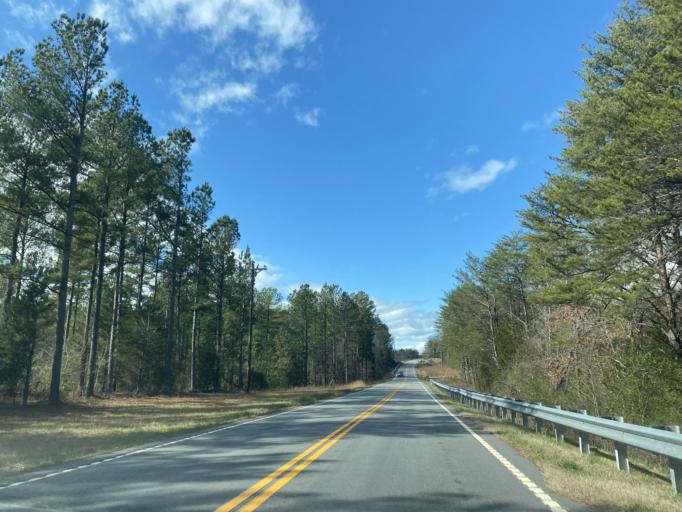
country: US
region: South Carolina
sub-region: Spartanburg County
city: Cowpens
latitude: 35.0948
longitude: -81.7473
